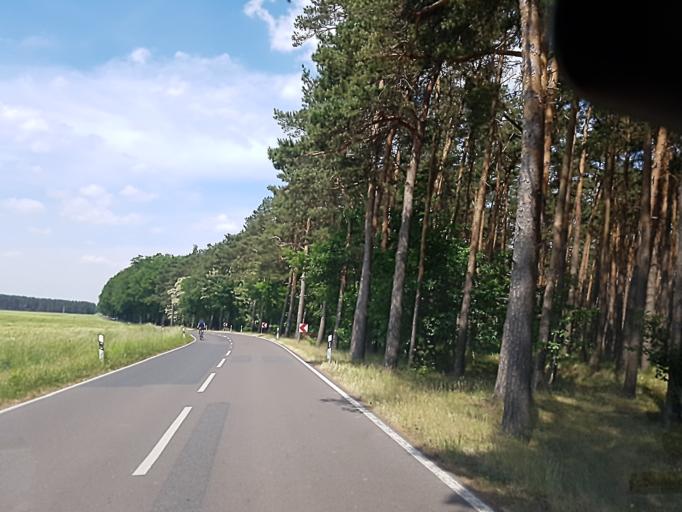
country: DE
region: Brandenburg
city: Gorzke
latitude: 52.1247
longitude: 12.3471
